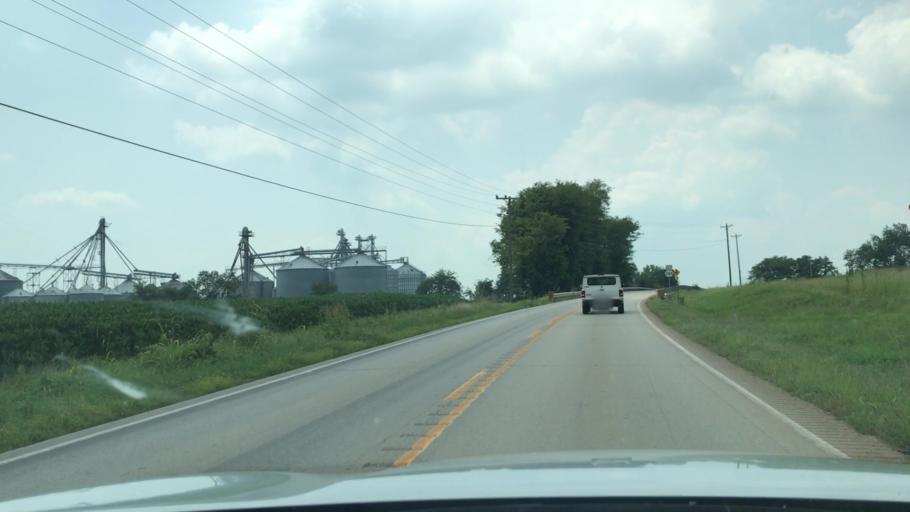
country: US
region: Kentucky
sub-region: Todd County
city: Guthrie
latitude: 36.6590
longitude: -87.1734
